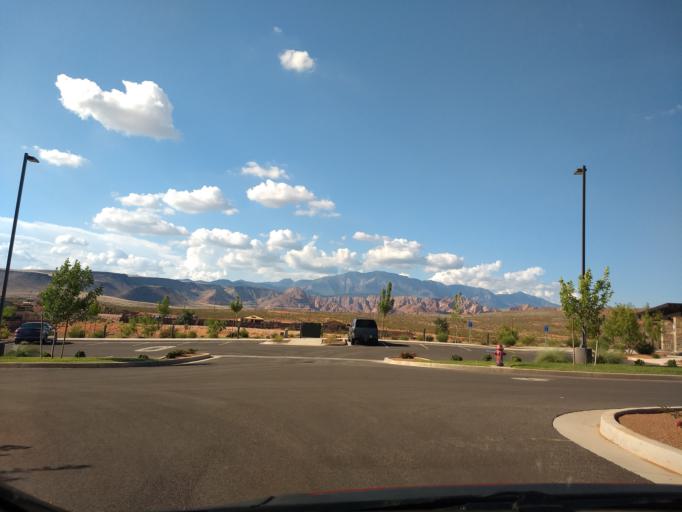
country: US
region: Utah
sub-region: Washington County
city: Washington
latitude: 37.1426
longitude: -113.5140
